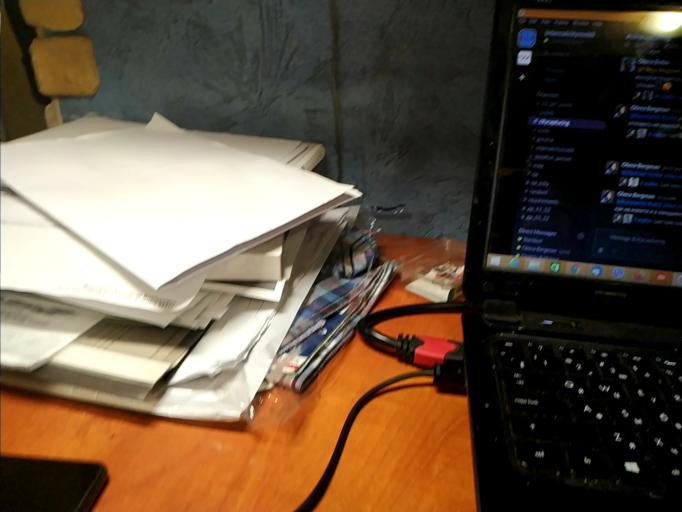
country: RU
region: Vologda
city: Suda
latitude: 58.8445
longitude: 37.5435
